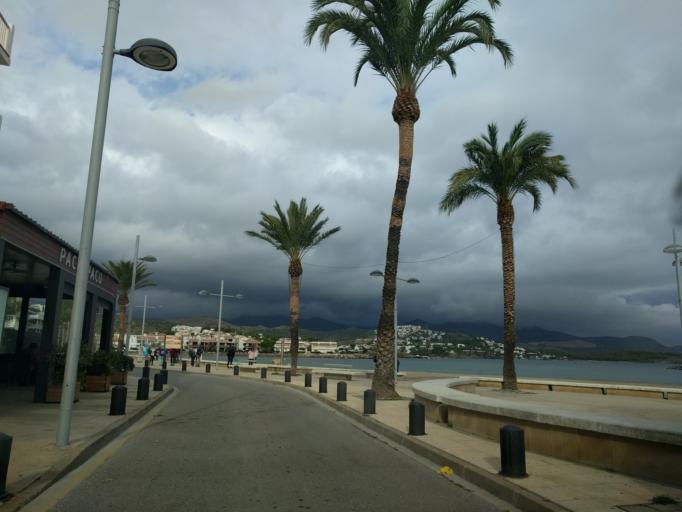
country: ES
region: Catalonia
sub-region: Provincia de Girona
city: Llanca
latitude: 42.3708
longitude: 3.1608
